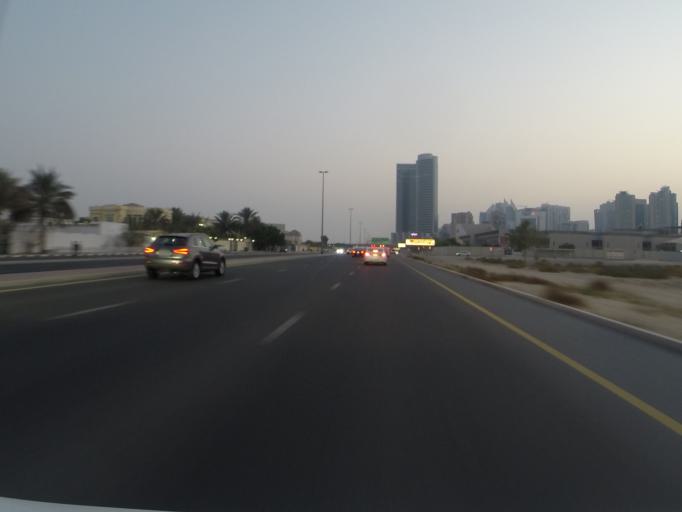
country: AE
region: Dubai
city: Dubai
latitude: 25.1018
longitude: 55.1858
